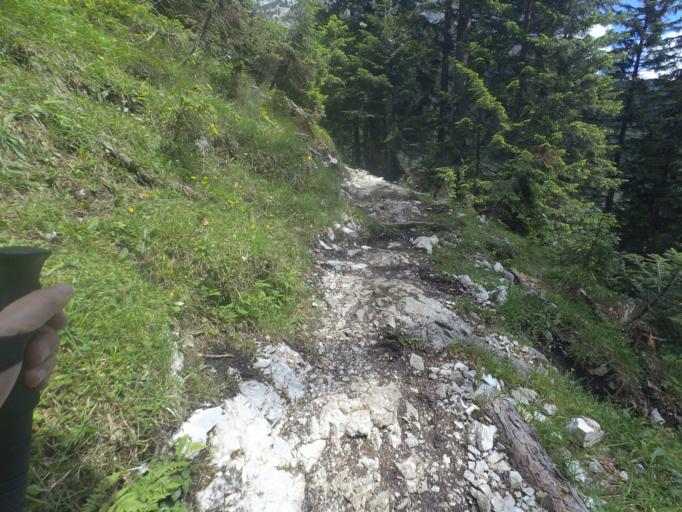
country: AT
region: Salzburg
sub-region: Politischer Bezirk Zell am See
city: Leogang
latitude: 47.4642
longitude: 12.7742
